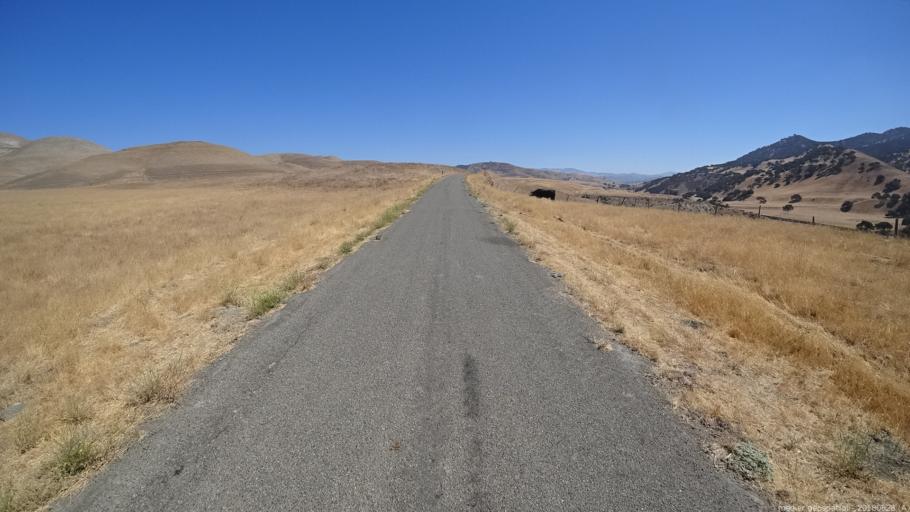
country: US
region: California
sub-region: San Luis Obispo County
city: San Miguel
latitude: 36.0617
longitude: -120.7984
